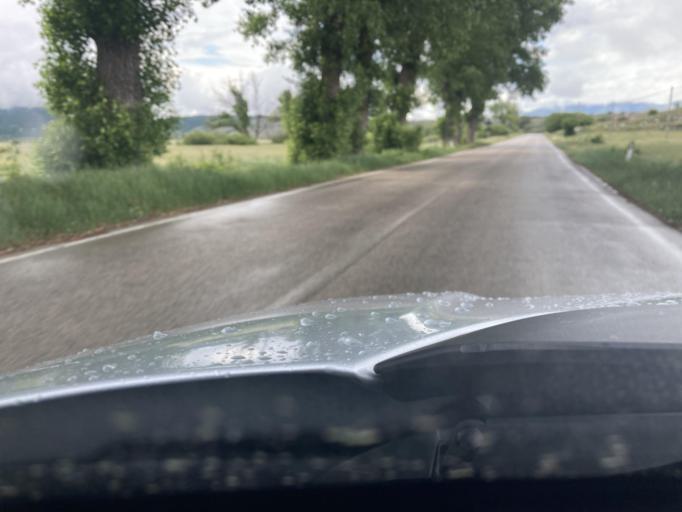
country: IT
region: Abruzzo
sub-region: Provincia dell' Aquila
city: Rocca di Mezzo
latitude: 42.2235
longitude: 13.5331
